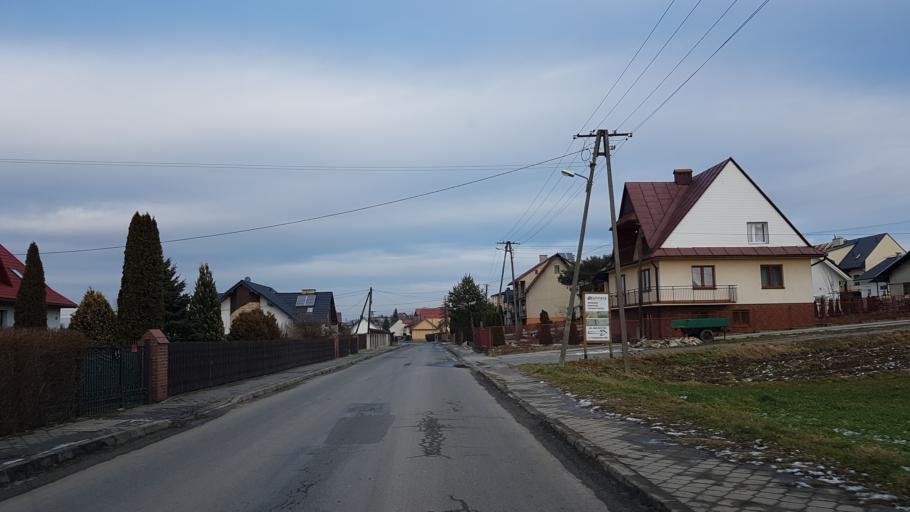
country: PL
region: Lesser Poland Voivodeship
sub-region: Powiat nowosadecki
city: Stary Sacz
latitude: 49.5479
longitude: 20.6271
